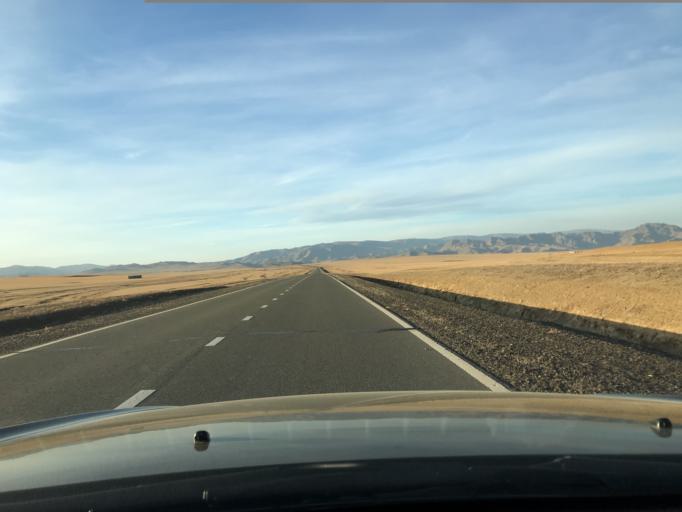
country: MN
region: Central Aimak
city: Arhust
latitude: 47.7435
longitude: 107.4591
